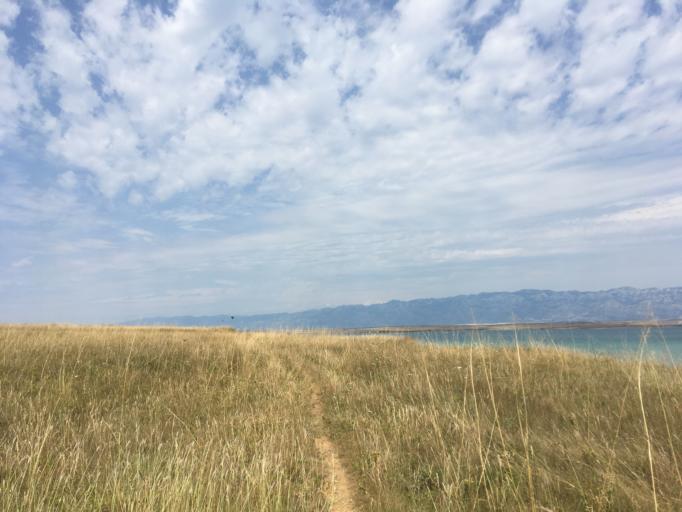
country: HR
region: Zadarska
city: Privlaka
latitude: 44.2698
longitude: 15.1514
